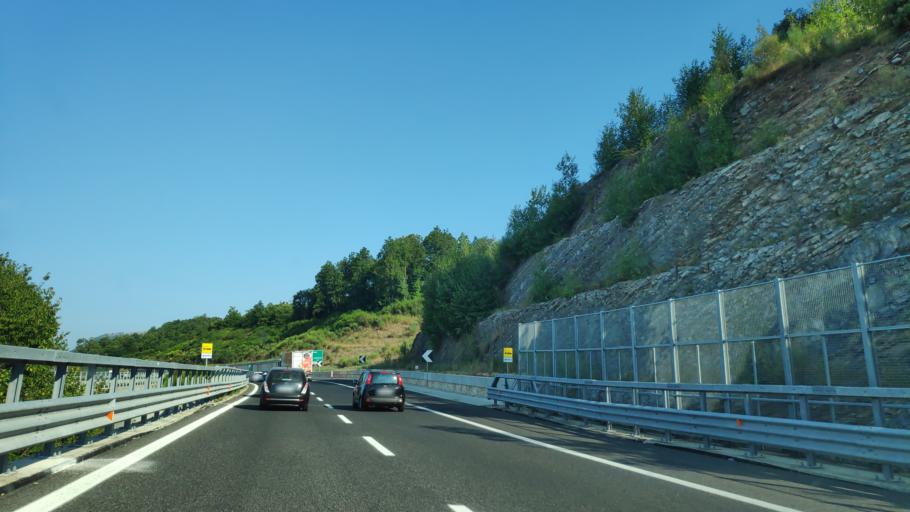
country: IT
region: Basilicate
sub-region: Provincia di Potenza
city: Lagonegro
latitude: 40.1279
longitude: 15.7750
